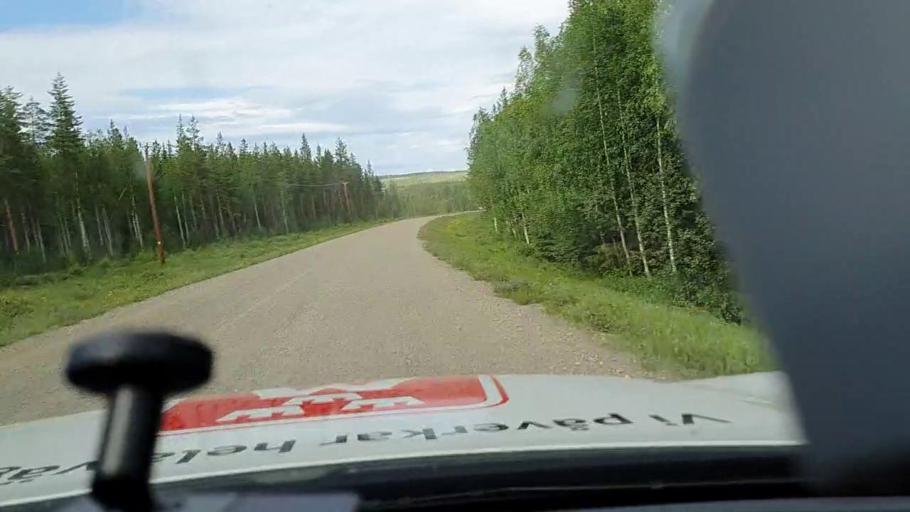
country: SE
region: Norrbotten
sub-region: Alvsbyns Kommun
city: AElvsbyn
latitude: 66.1452
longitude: 21.0208
